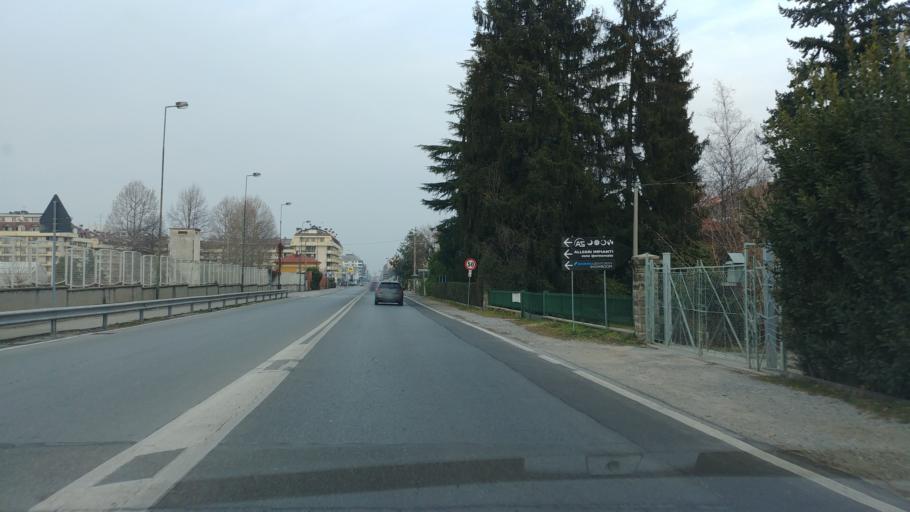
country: IT
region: Piedmont
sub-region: Provincia di Cuneo
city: Cuneo
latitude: 44.3726
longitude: 7.5305
